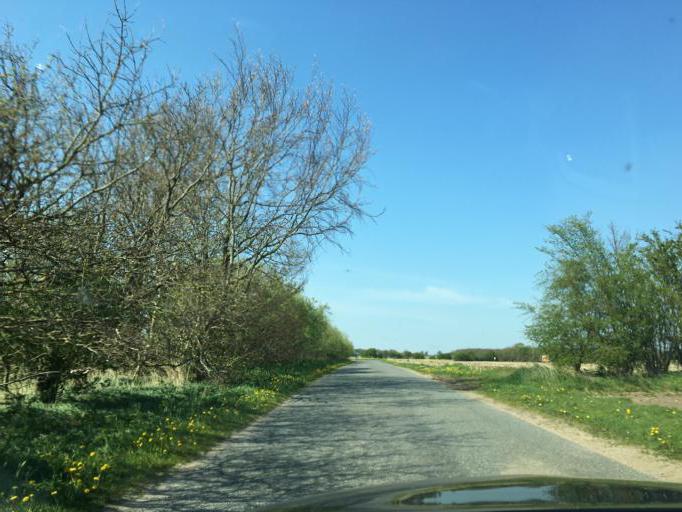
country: DK
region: South Denmark
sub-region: Esbjerg Kommune
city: Bramming
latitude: 55.4969
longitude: 8.6693
